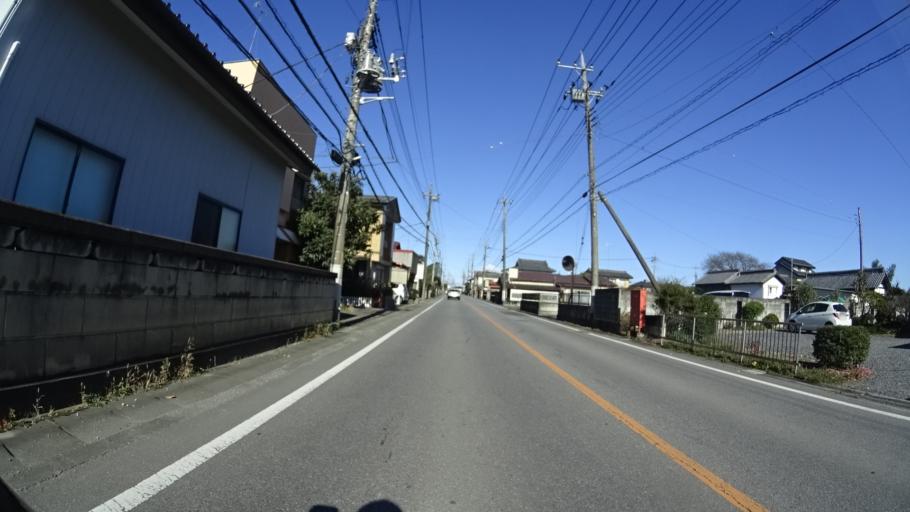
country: JP
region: Tochigi
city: Tochigi
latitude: 36.4127
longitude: 139.7470
